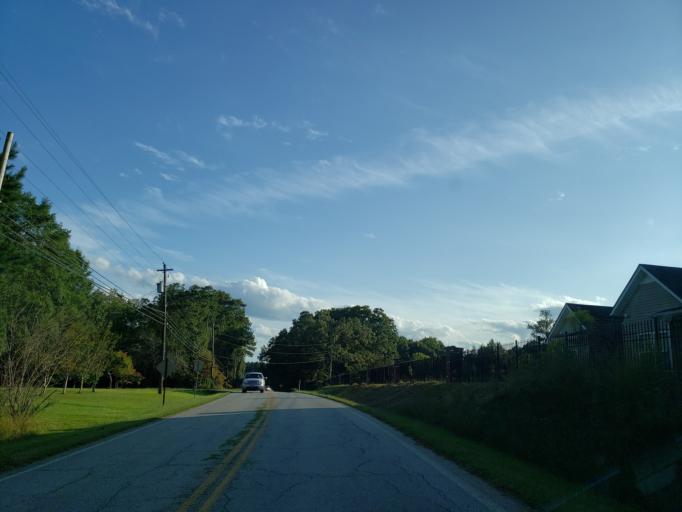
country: US
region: Georgia
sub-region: Carroll County
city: Temple
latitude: 33.7349
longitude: -85.0344
